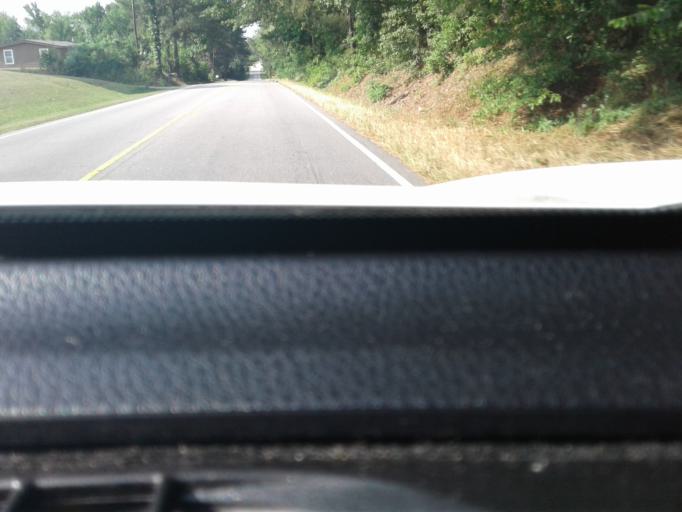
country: US
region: North Carolina
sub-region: Johnston County
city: Benson
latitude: 35.4108
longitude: -78.5404
